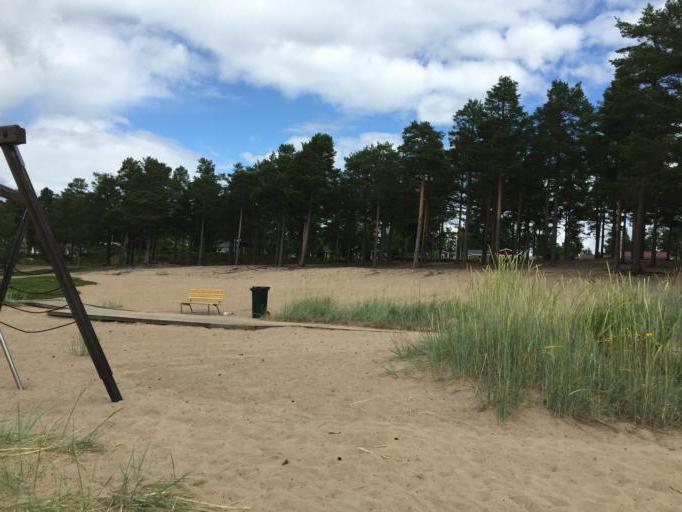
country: SE
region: Gaevleborg
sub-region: Hudiksvalls Kommun
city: Hudiksvall
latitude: 61.7176
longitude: 17.1755
